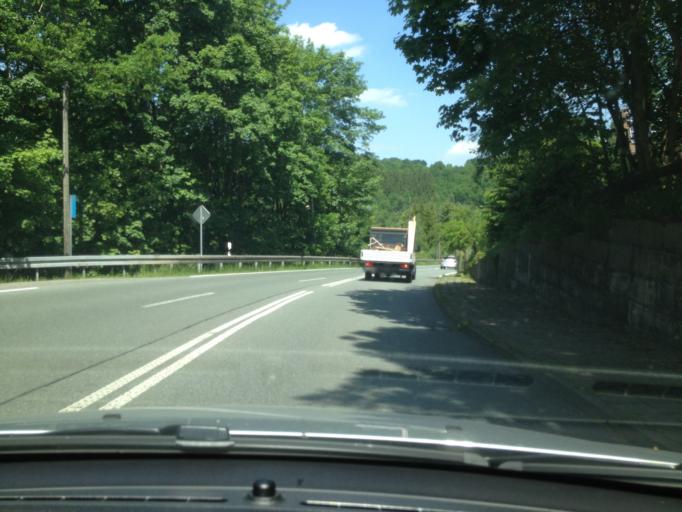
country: DE
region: Saxony
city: Burkhardtsdorf
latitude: 50.7297
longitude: 12.9306
